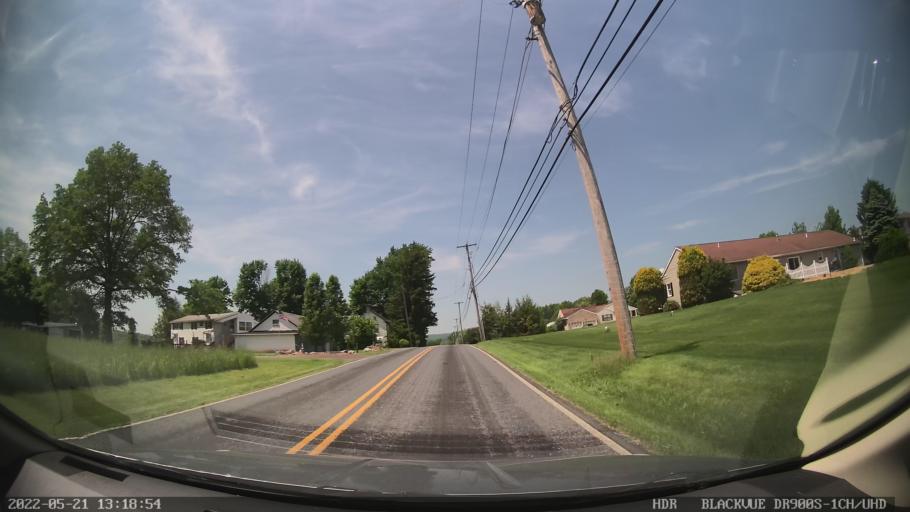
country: US
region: Pennsylvania
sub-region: Berks County
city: Bally
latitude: 40.3702
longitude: -75.5975
